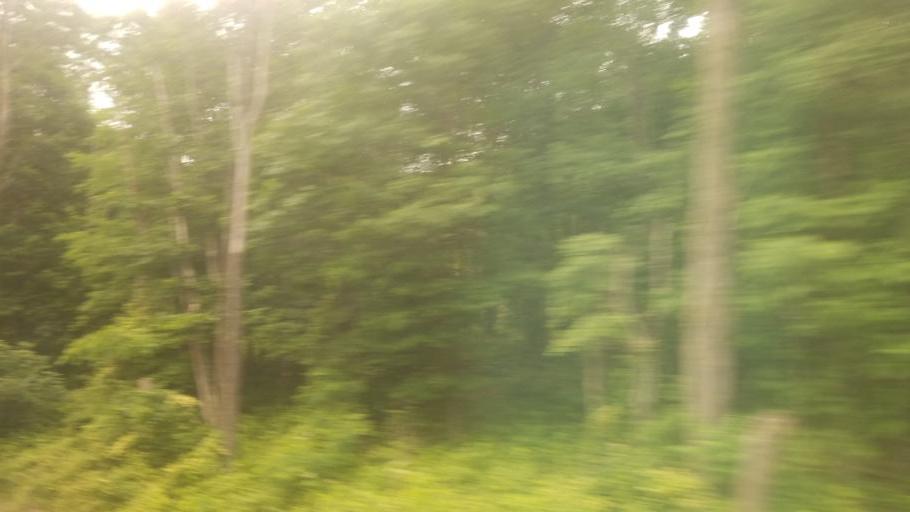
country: US
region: West Virginia
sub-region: Morgan County
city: Berkeley Springs
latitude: 39.5787
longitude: -78.4001
